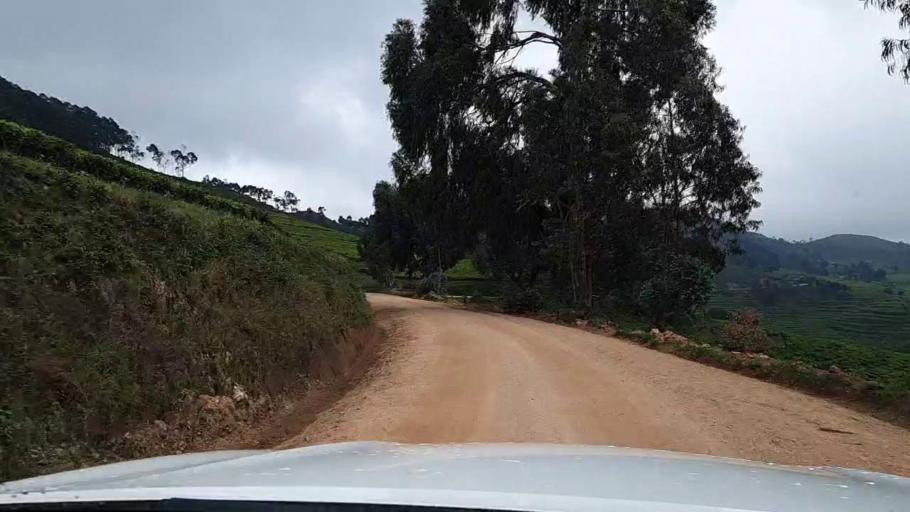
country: RW
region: Western Province
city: Kibuye
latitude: -2.2958
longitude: 29.3837
